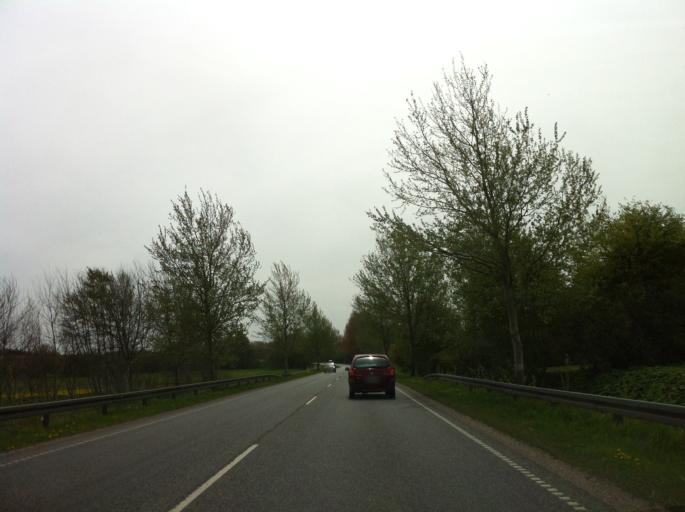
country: DK
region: Capital Region
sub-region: Frederikssund Kommune
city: Slangerup
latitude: 55.8418
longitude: 12.1574
